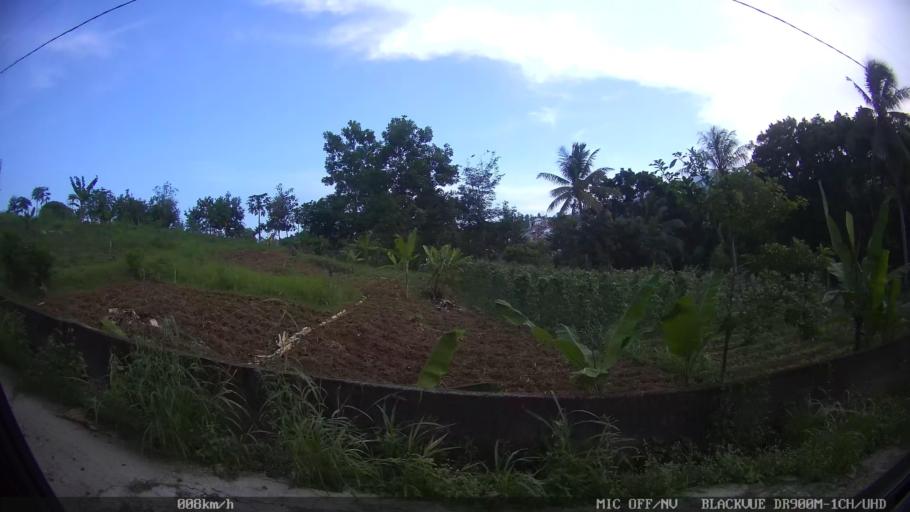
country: ID
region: Lampung
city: Kedaton
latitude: -5.3928
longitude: 105.1976
